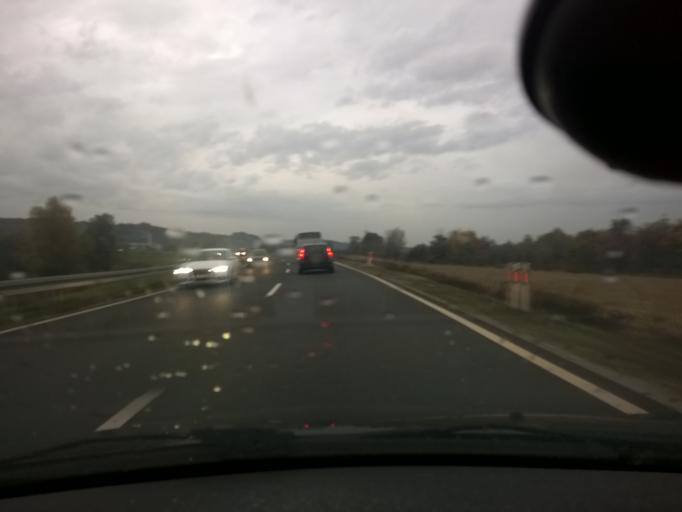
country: HR
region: Zagrebacka
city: Pojatno
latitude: 45.8994
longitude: 15.8161
